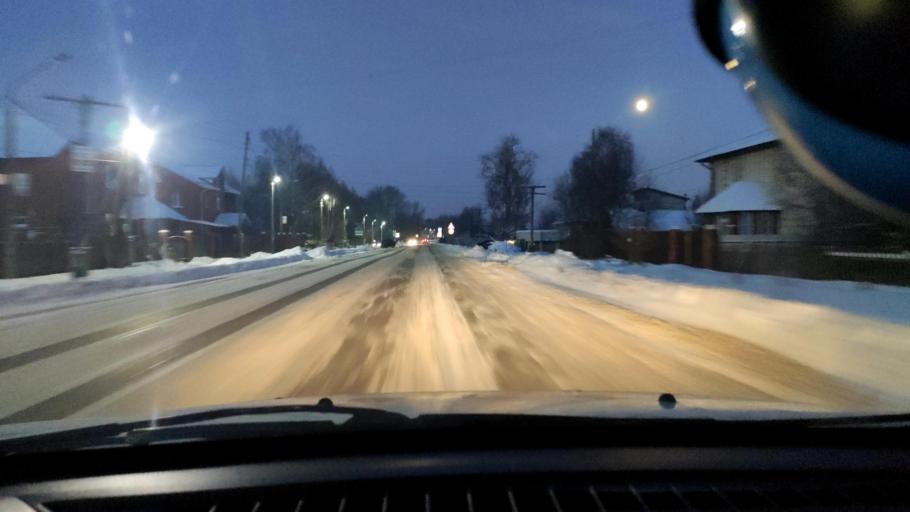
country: RU
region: Perm
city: Kultayevo
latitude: 57.8915
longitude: 55.9311
